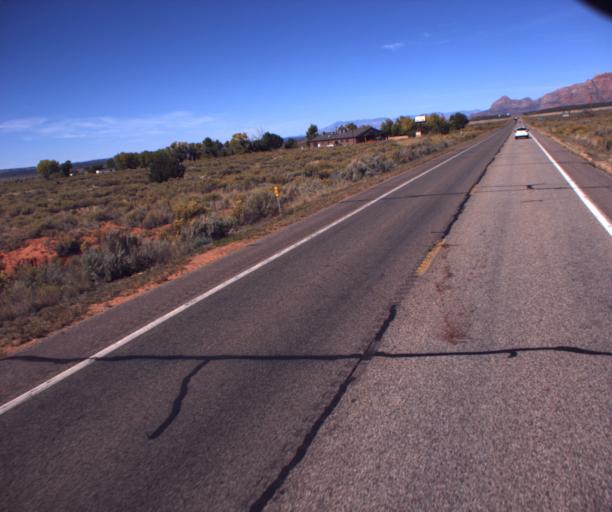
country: US
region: Arizona
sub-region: Mohave County
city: Colorado City
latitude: 36.9289
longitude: -112.9420
